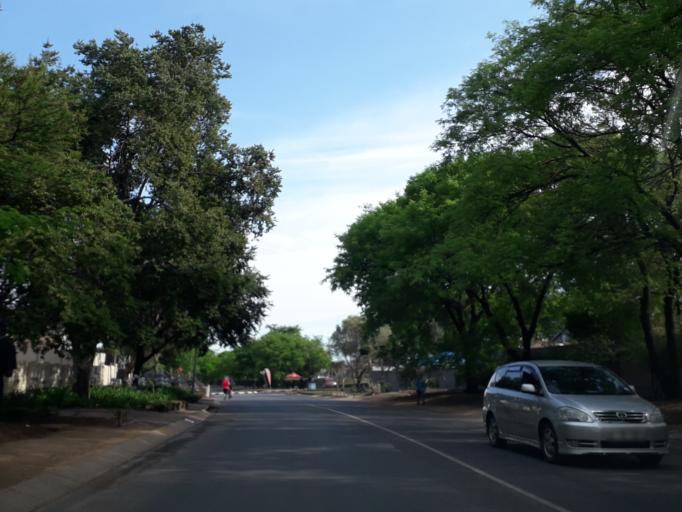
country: ZA
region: Gauteng
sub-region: City of Johannesburg Metropolitan Municipality
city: Diepsloot
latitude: -26.0298
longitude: 28.0038
